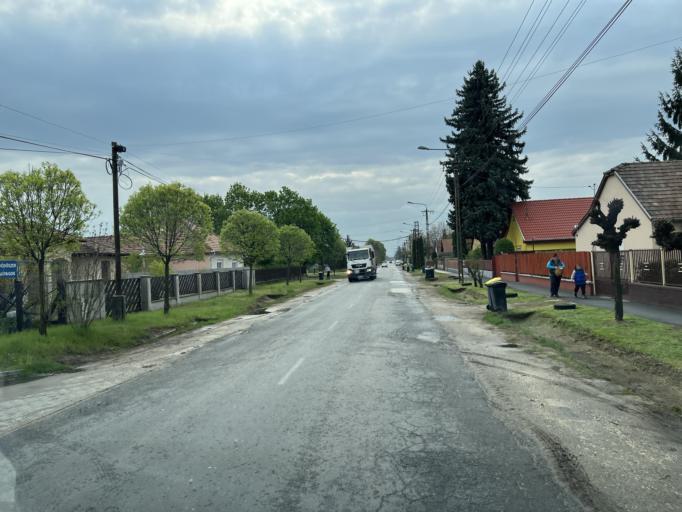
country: HU
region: Pest
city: Danszentmiklos
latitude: 47.2133
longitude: 19.5452
